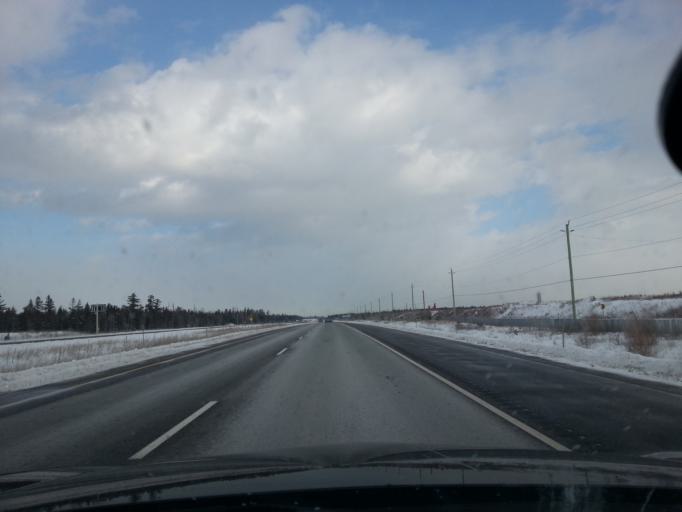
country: CA
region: Ontario
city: Bells Corners
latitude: 45.2333
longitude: -75.9893
